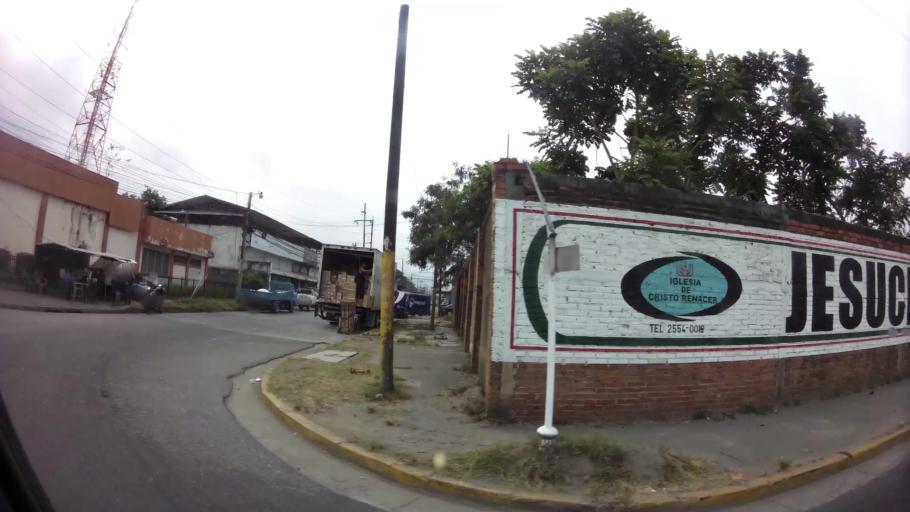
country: HN
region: Yoro
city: El Progreso
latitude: 15.4050
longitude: -87.8072
